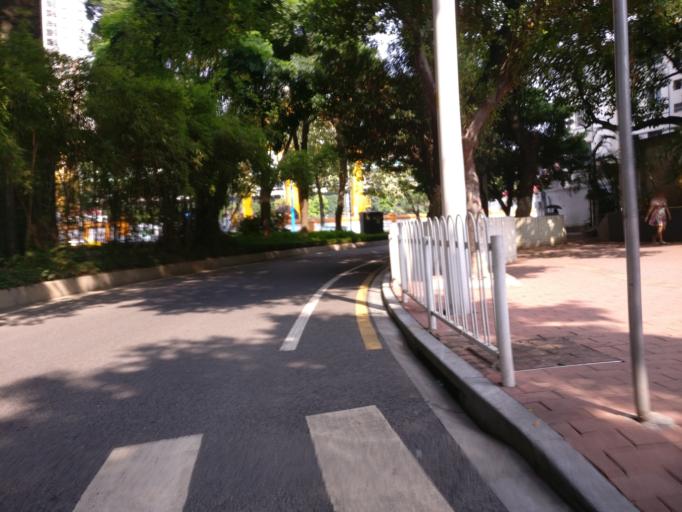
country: CN
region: Guangdong
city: Guangzhou
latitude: 23.1294
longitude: 113.2729
